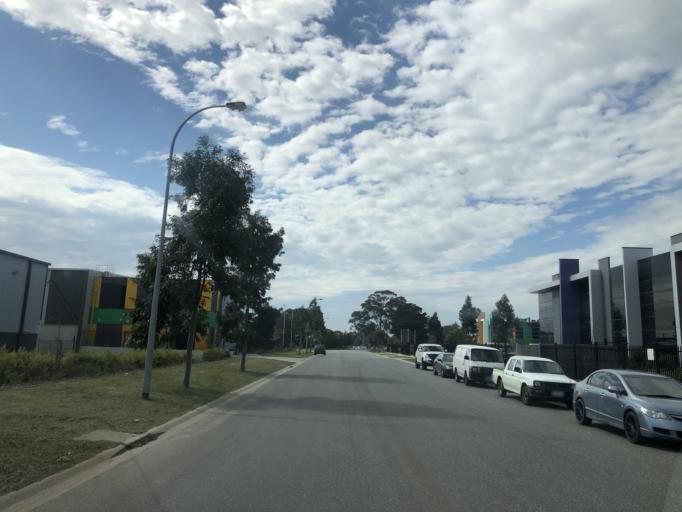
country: AU
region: Victoria
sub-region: Casey
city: Hampton Park
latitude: -38.0414
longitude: 145.2143
